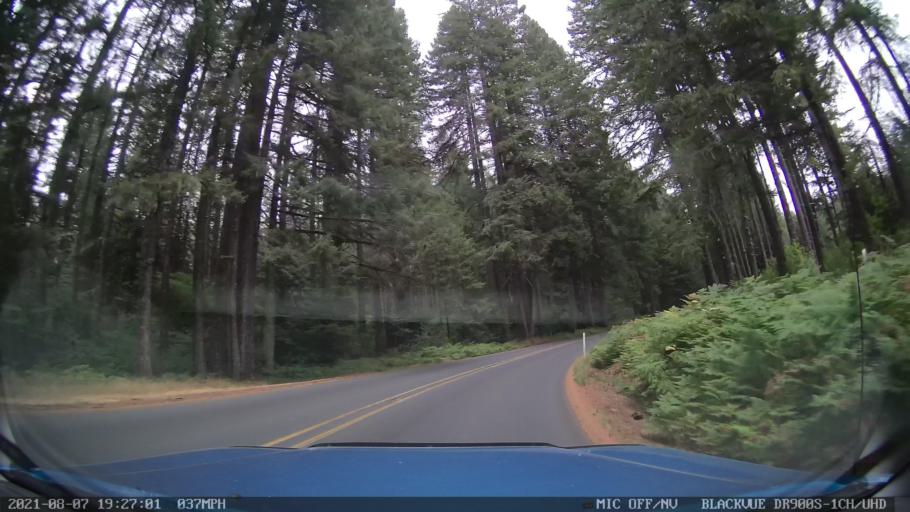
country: US
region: Oregon
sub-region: Linn County
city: Lyons
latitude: 44.8777
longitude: -122.6512
